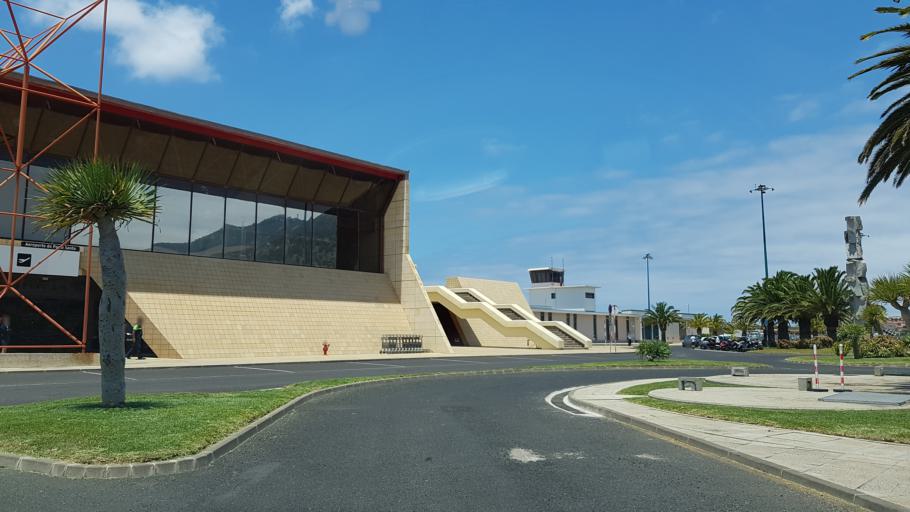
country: PT
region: Madeira
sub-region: Porto Santo
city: Vila de Porto Santo
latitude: 33.0703
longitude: -16.3449
